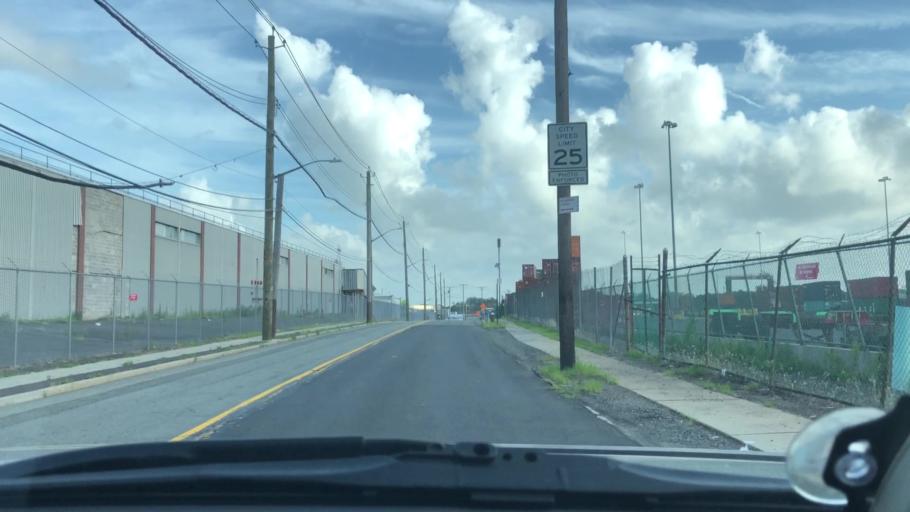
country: US
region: New York
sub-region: Richmond County
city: Bloomfield
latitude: 40.6403
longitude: -74.1799
